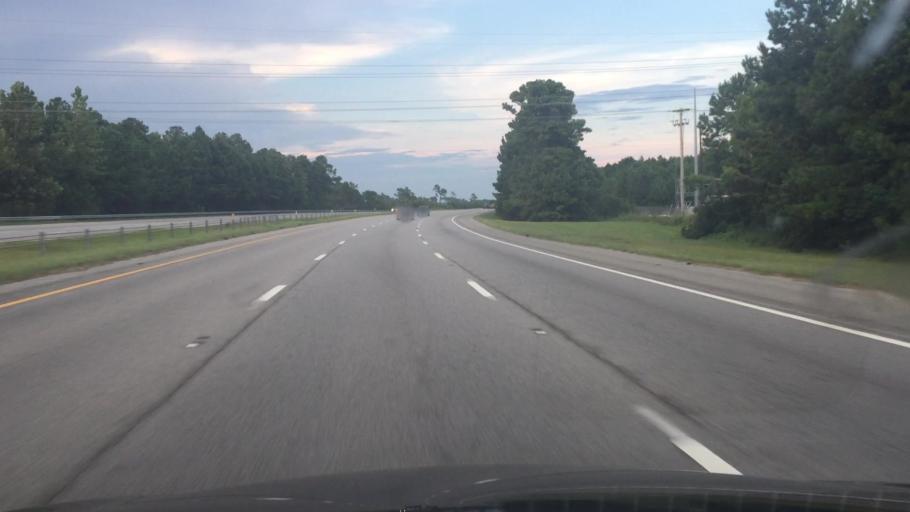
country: US
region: South Carolina
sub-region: Horry County
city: Myrtle Beach
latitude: 33.7646
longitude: -78.8344
